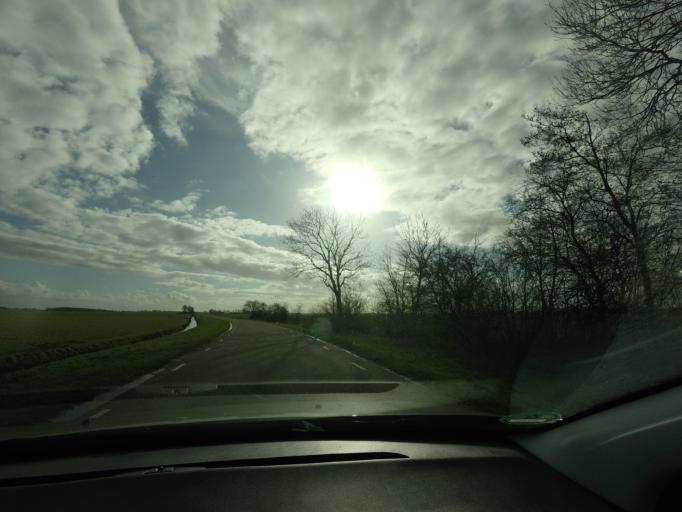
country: NL
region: Friesland
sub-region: Gemeente Boarnsterhim
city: Jirnsum
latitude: 53.0637
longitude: 5.7413
